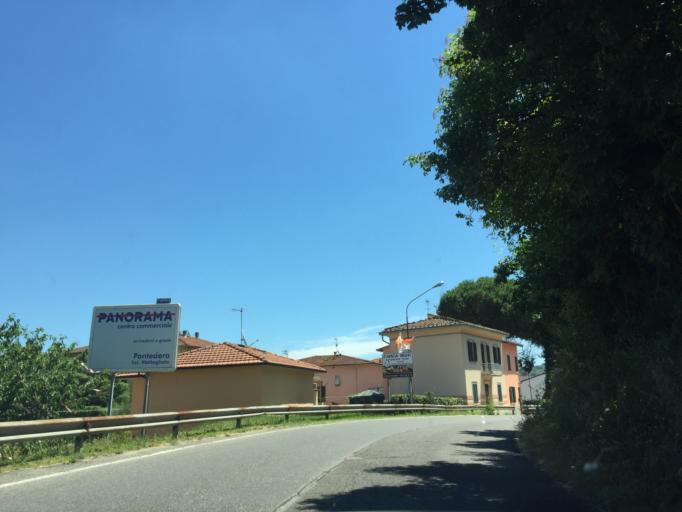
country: IT
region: Tuscany
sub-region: Province of Pisa
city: San Miniato
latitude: 43.6881
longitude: 10.7891
